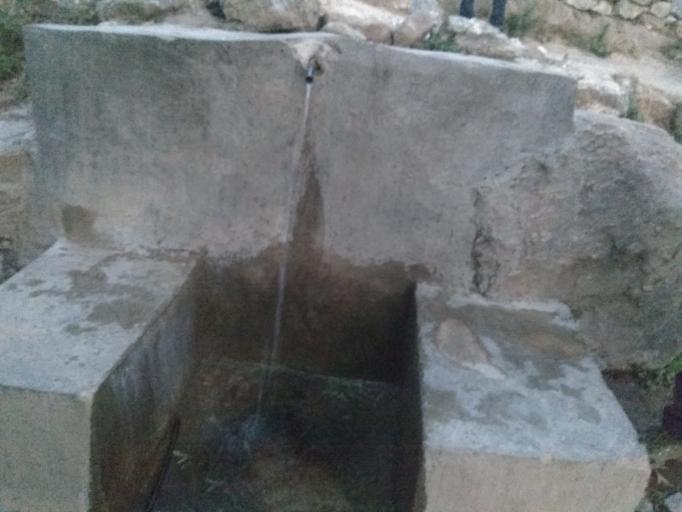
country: NP
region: Far Western
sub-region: Seti Zone
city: Achham
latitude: 29.2287
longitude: 81.6319
